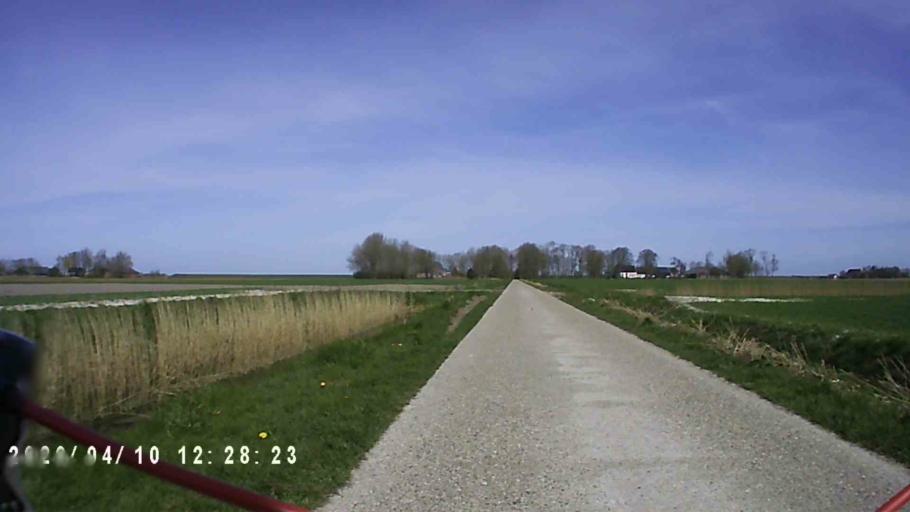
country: NL
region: Groningen
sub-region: Gemeente De Marne
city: Ulrum
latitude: 53.3987
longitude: 6.4096
